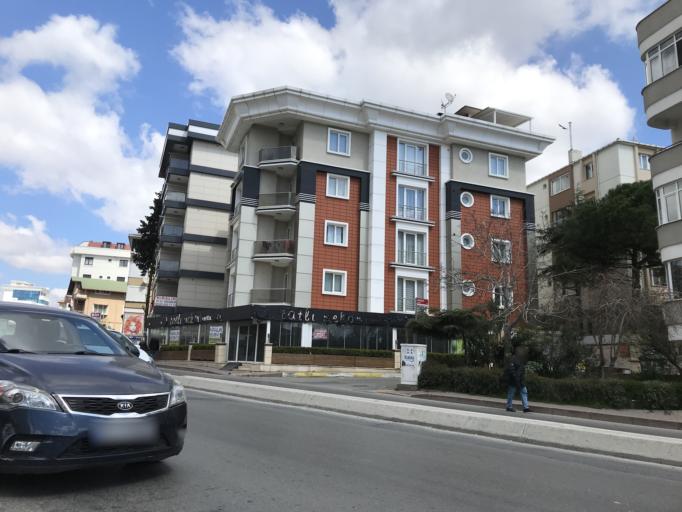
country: TR
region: Istanbul
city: Maltepe
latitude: 40.9298
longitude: 29.1347
